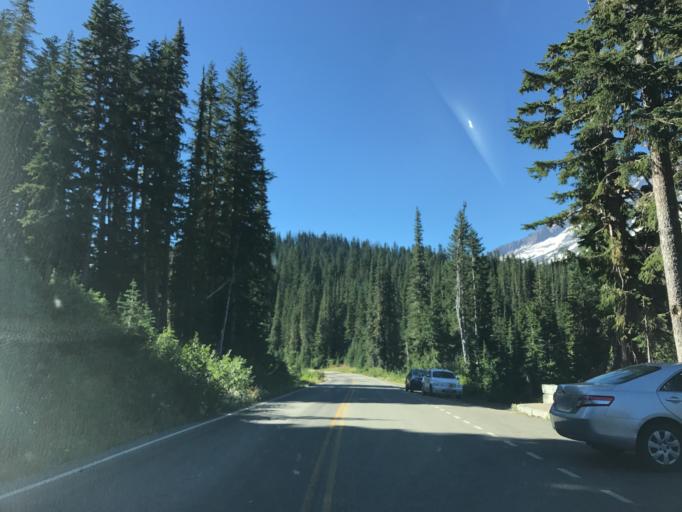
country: US
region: Washington
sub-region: Pierce County
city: Buckley
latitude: 46.7686
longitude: -121.7320
